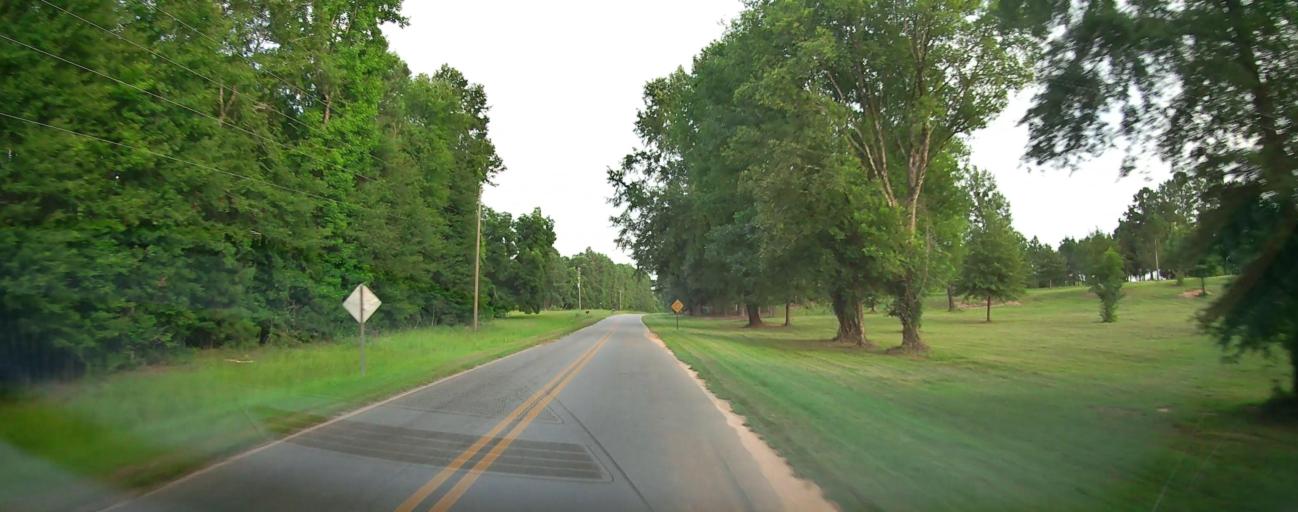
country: US
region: Georgia
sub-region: Crawford County
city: Roberta
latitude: 32.6662
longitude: -84.0670
